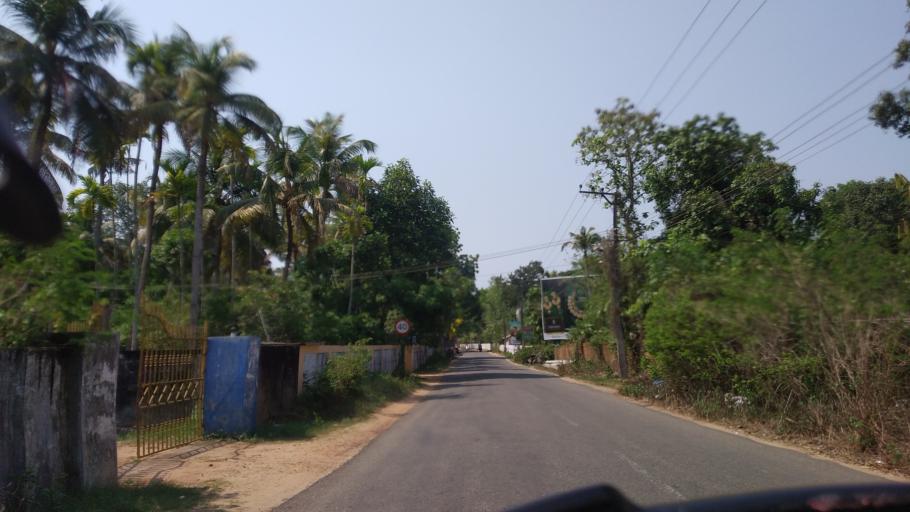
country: IN
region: Kerala
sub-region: Thrissur District
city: Kodungallur
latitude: 10.2627
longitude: 76.1439
